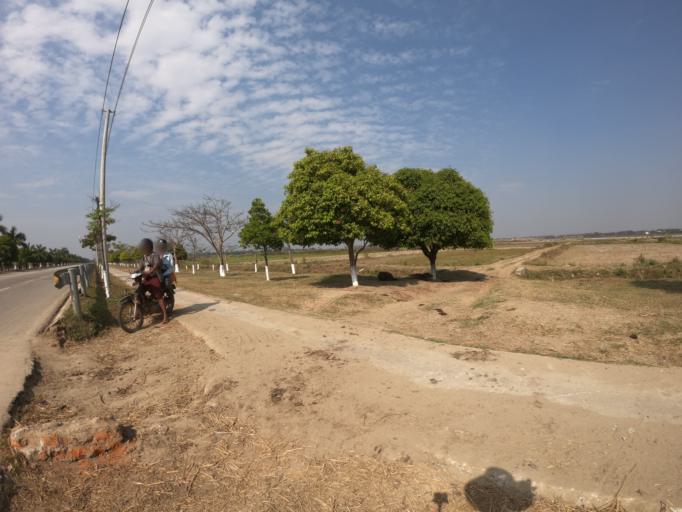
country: MM
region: Mandalay
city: Pyinmana
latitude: 19.6157
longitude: 96.1714
